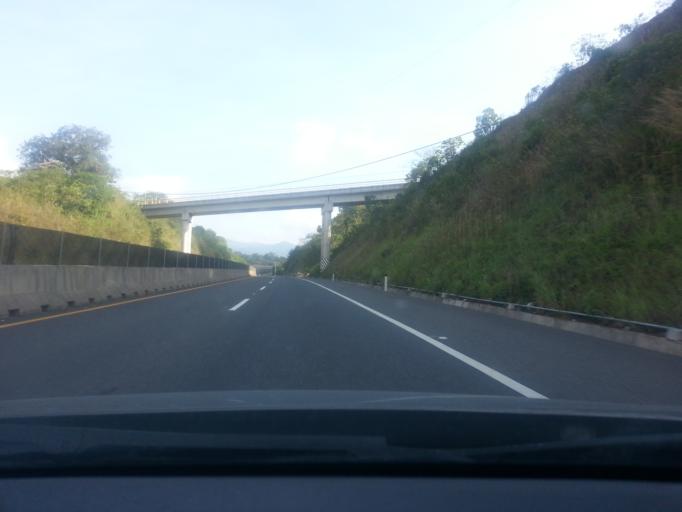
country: MX
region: Puebla
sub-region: Xicotepec
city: San Lorenzo
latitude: 20.3961
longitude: -97.9454
